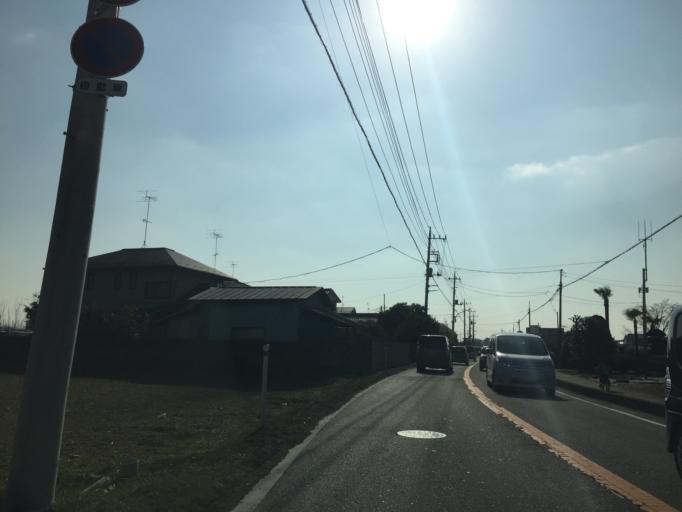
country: JP
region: Saitama
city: Oi
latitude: 35.8658
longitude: 139.5555
